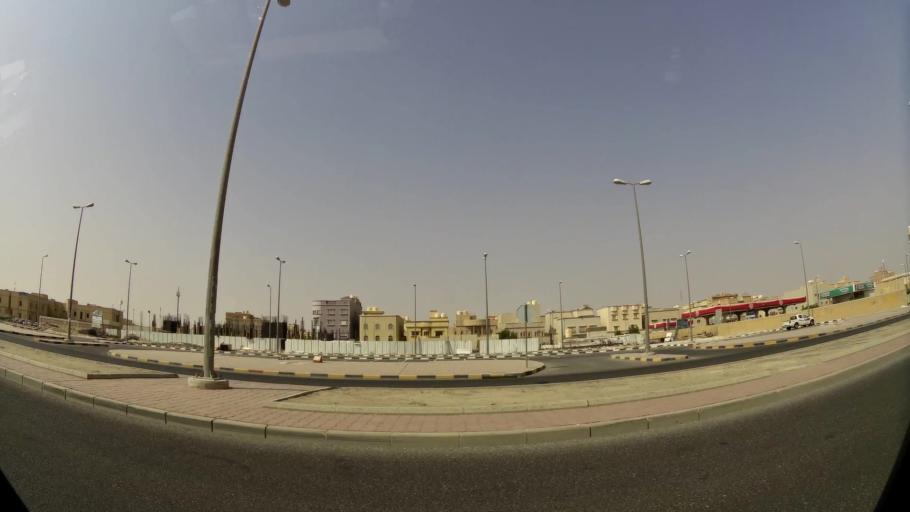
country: KW
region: Muhafazat al Jahra'
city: Al Jahra'
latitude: 29.3076
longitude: 47.7006
